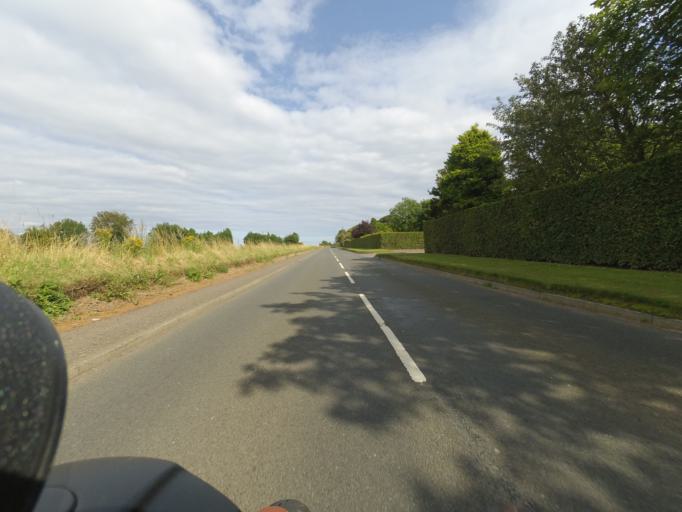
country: GB
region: Scotland
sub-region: Angus
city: Montrose
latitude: 56.7234
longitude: -2.4922
